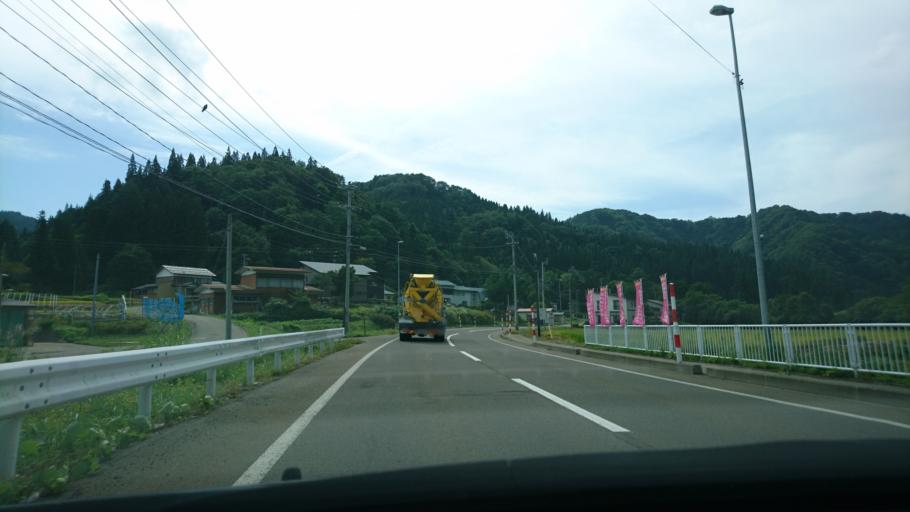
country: JP
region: Akita
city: Yuzawa
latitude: 39.1735
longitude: 140.6808
